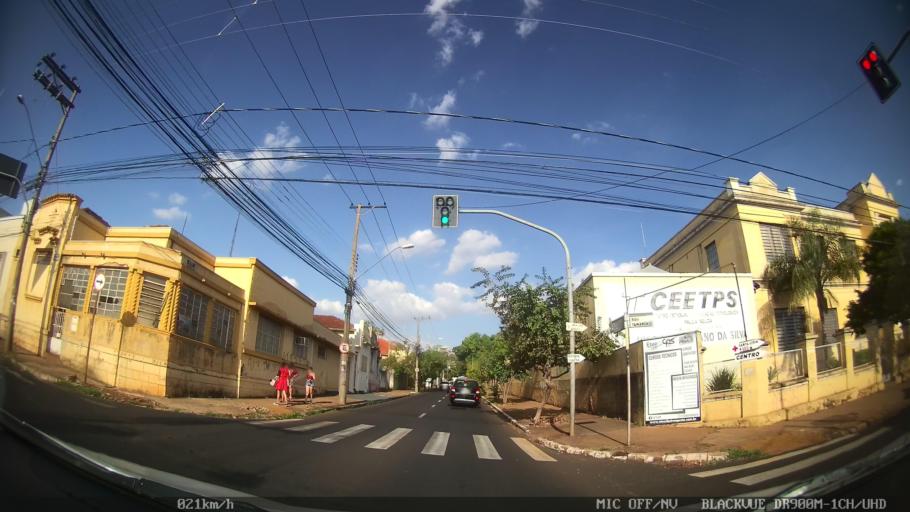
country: BR
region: Sao Paulo
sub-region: Ribeirao Preto
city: Ribeirao Preto
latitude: -21.1692
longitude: -47.8027
